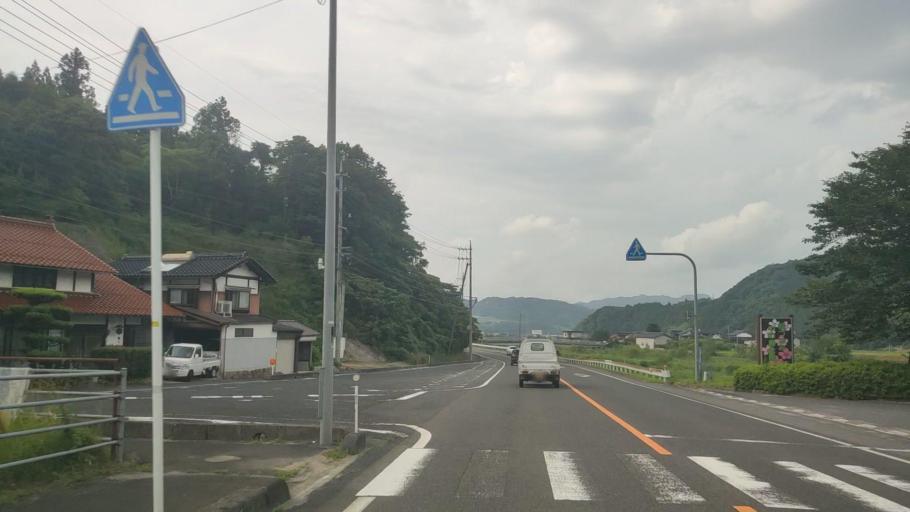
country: JP
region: Tottori
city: Kurayoshi
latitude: 35.3891
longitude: 133.8569
